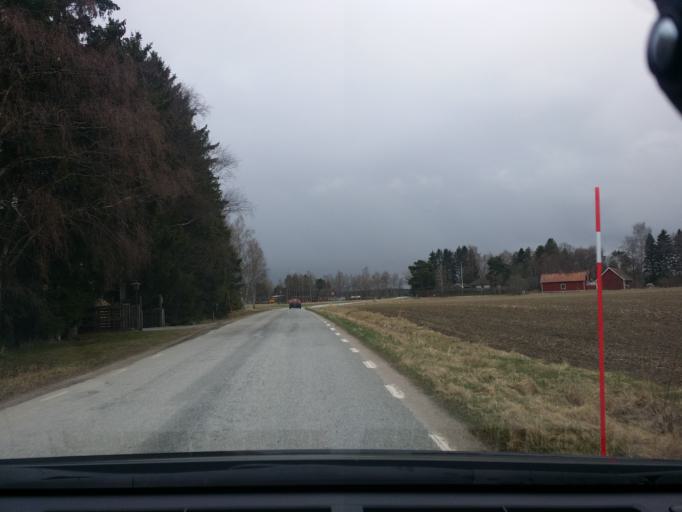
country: SE
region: Uppsala
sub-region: Enkopings Kommun
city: Enkoping
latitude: 59.6804
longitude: 17.0393
